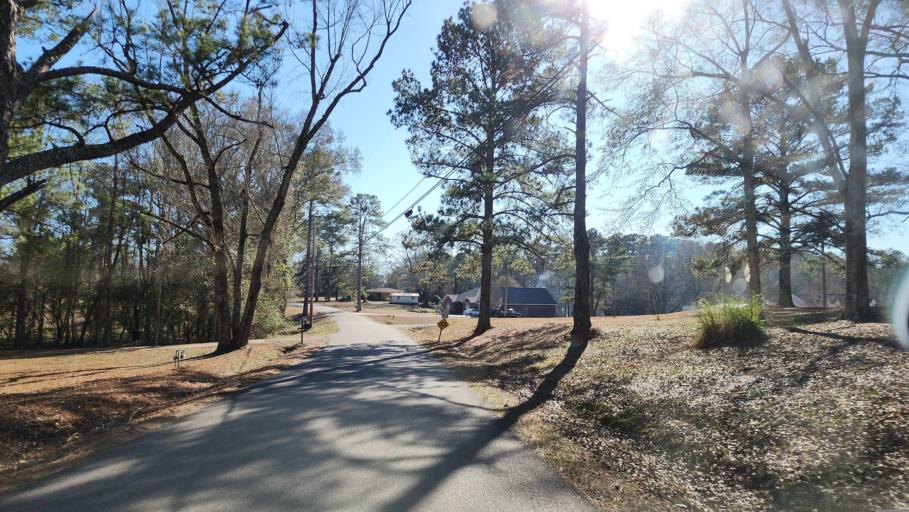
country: US
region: Mississippi
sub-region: Jones County
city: Laurel
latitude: 31.7086
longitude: -89.0928
